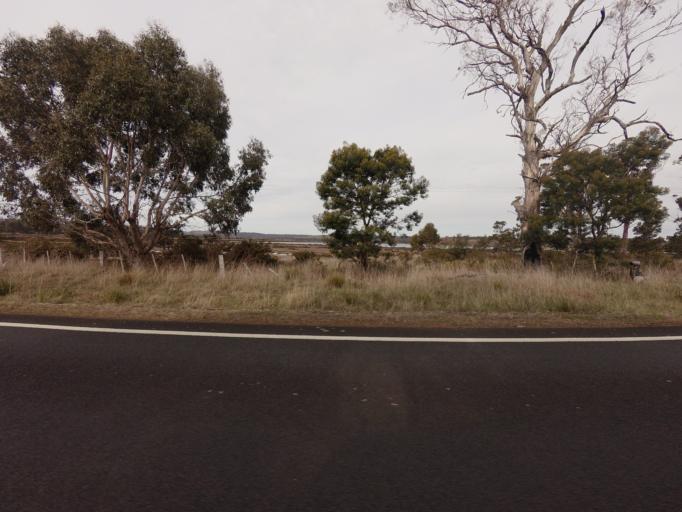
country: AU
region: Tasmania
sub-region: Sorell
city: Sorell
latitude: -42.3414
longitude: 147.9312
